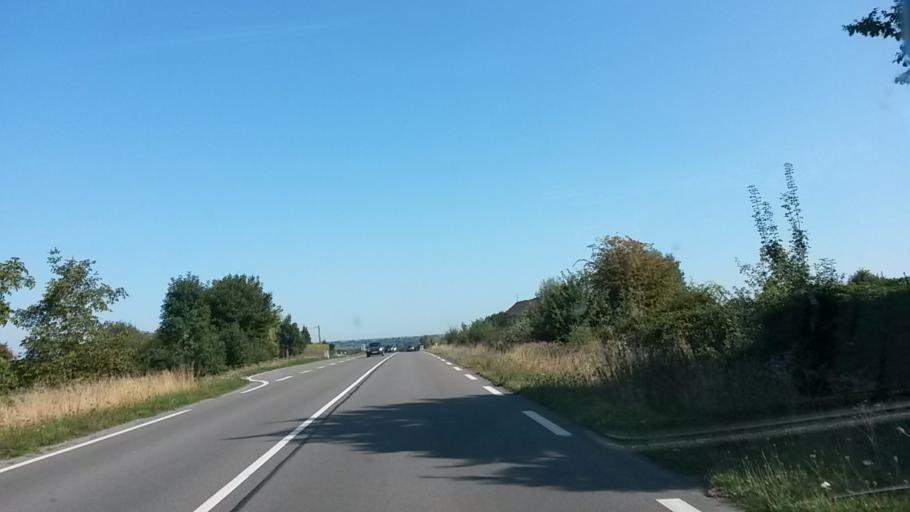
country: FR
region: Picardie
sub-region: Departement de l'Aisne
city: La Flamengrie
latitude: 50.0390
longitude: 3.9253
